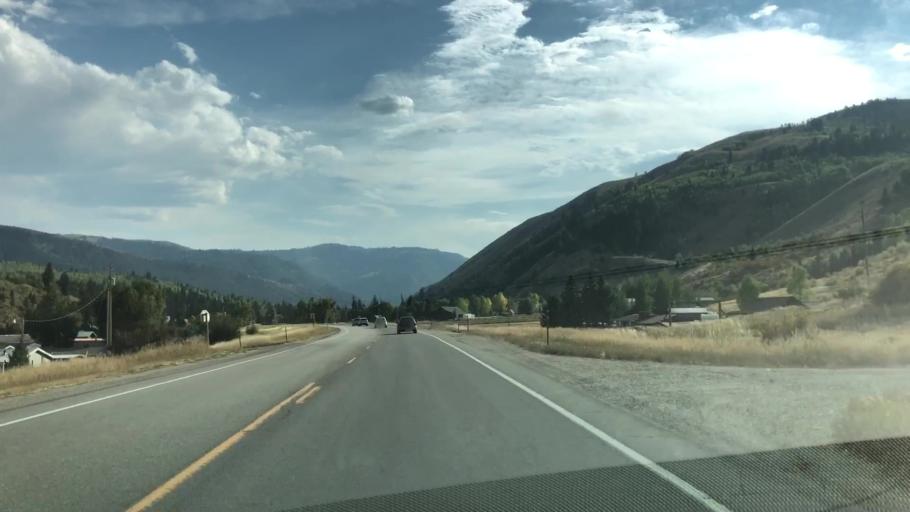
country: US
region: Wyoming
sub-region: Teton County
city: Hoback
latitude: 43.3489
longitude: -110.7212
